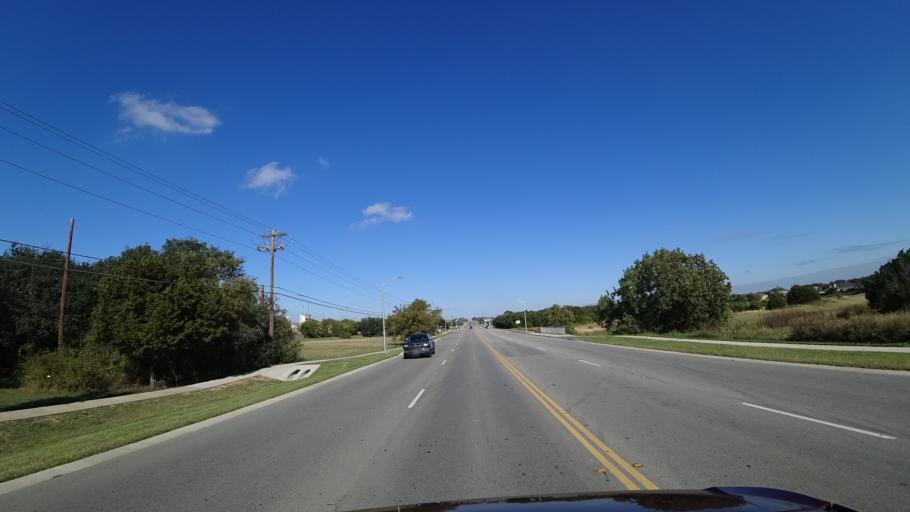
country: US
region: Texas
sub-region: Williamson County
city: Cedar Park
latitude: 30.5331
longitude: -97.8463
